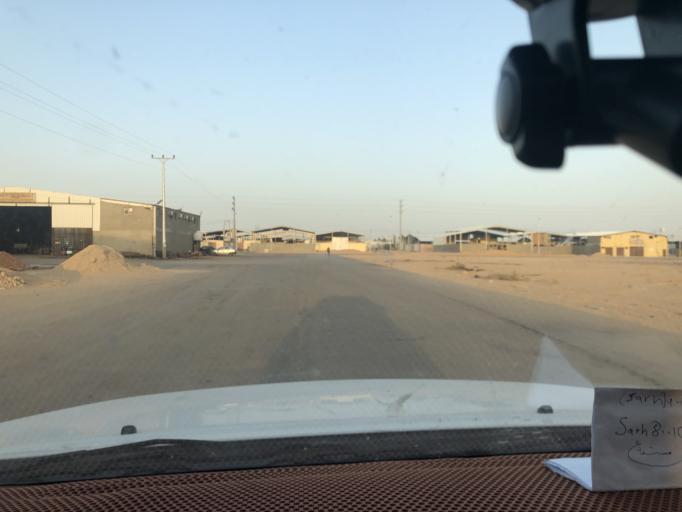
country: SA
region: Ar Riyad
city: As Sulayyil
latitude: 20.4072
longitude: 44.8711
